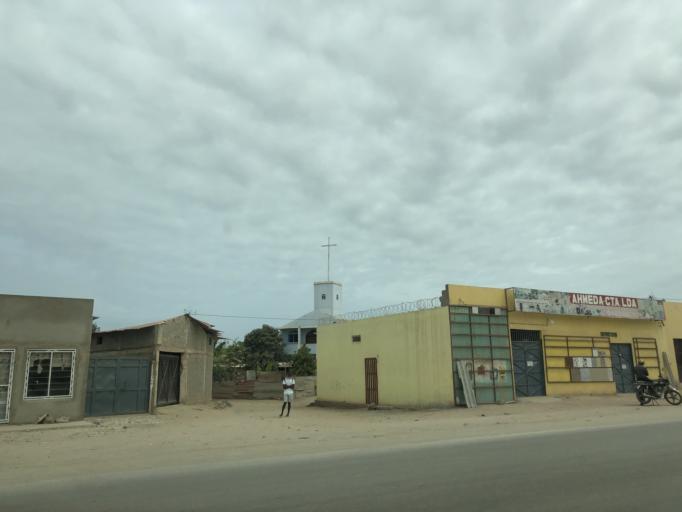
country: AO
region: Cuanza Sul
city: Sumbe
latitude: -11.1835
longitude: 13.8622
